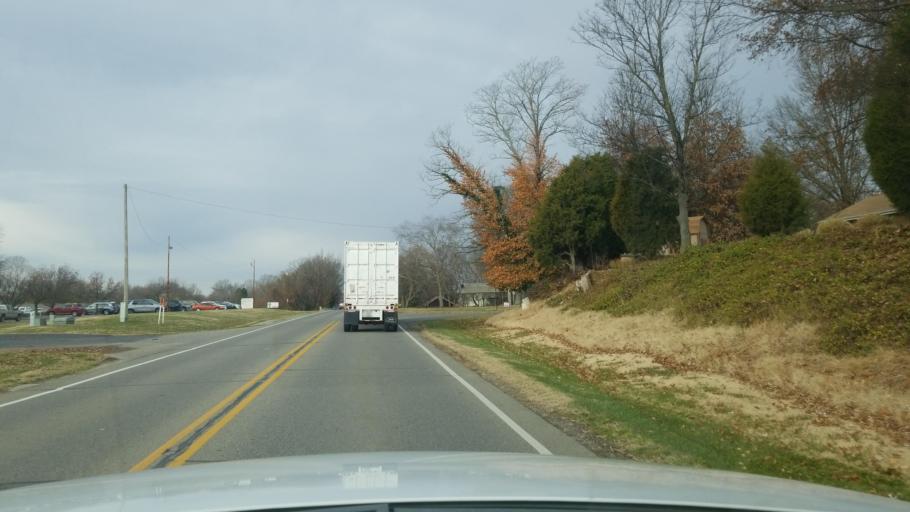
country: US
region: Indiana
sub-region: Posey County
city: Mount Vernon
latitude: 37.9284
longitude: -87.9206
